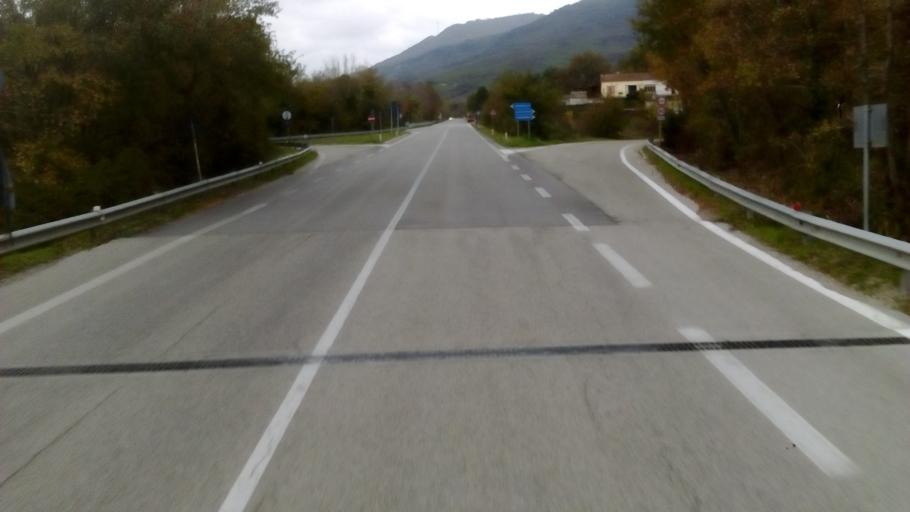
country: IT
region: Abruzzo
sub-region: Provincia di Chieti
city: Tufillo
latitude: 41.8912
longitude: 14.6123
